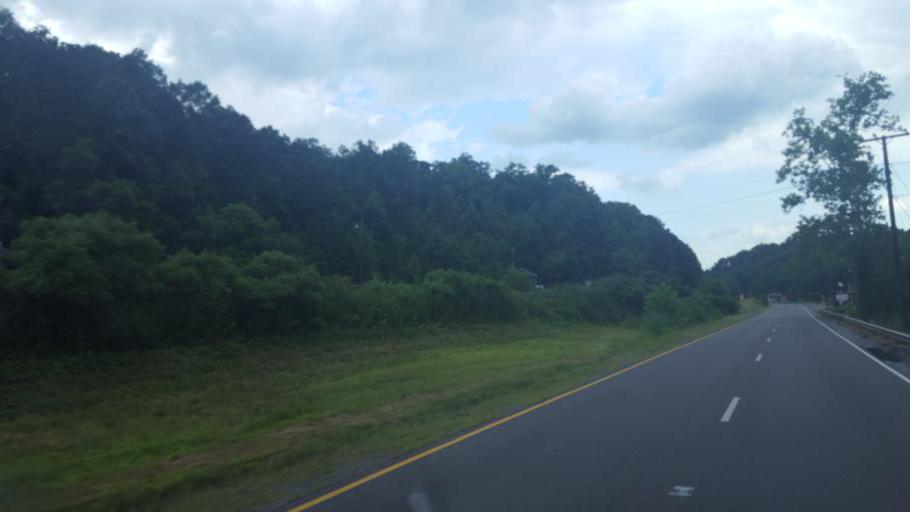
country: US
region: Virginia
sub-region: Wise County
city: Pound
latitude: 37.0945
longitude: -82.6002
